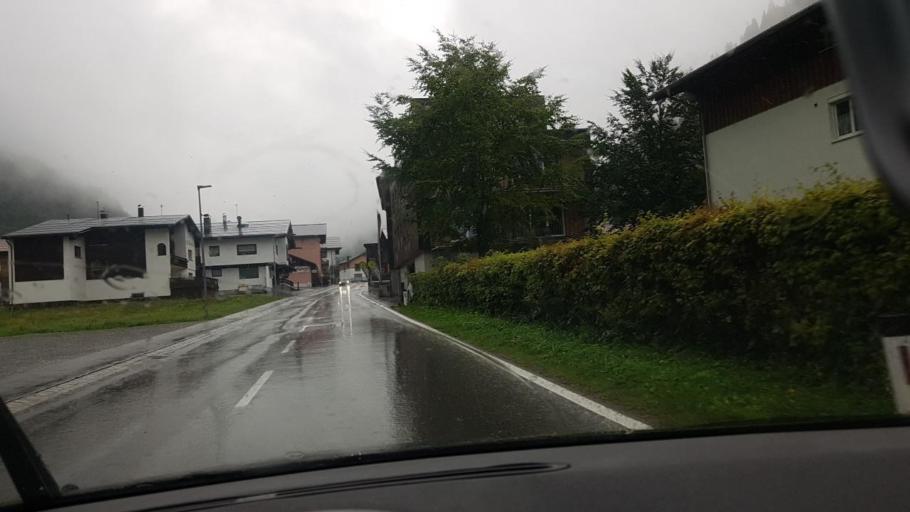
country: AT
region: Vorarlberg
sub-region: Politischer Bezirk Bludenz
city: Klosterle
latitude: 47.1314
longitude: 10.0872
